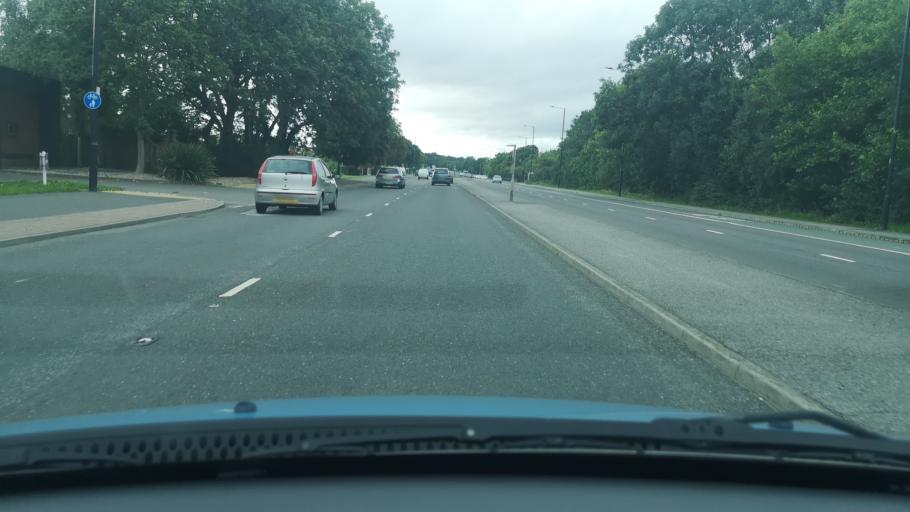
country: GB
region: England
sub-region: Doncaster
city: Bentley
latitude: 53.5384
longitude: -1.1660
